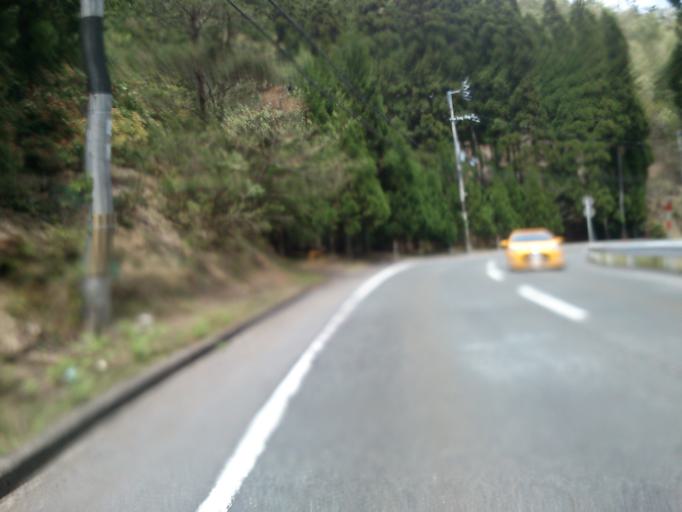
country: JP
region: Kyoto
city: Kameoka
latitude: 35.1998
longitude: 135.6290
